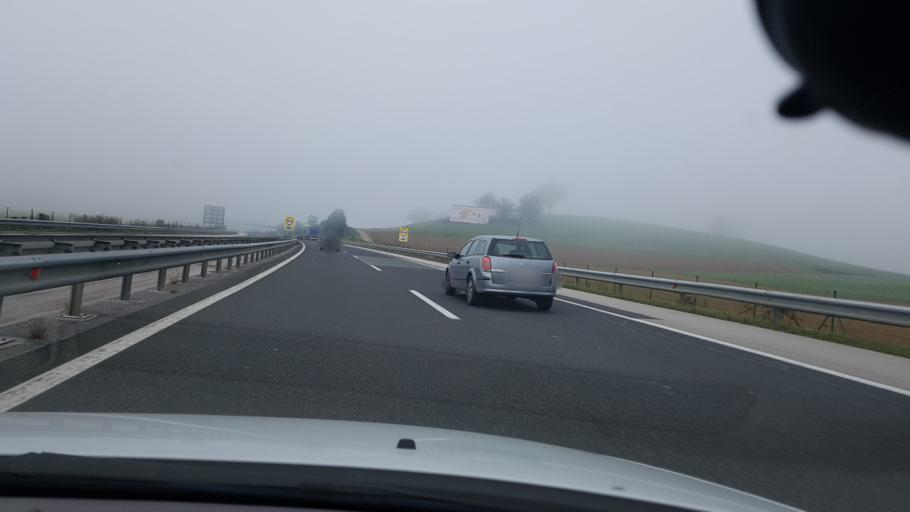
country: SI
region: Ivancna Gorica
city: Sentvid pri Sticni
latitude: 45.9252
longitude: 14.8751
